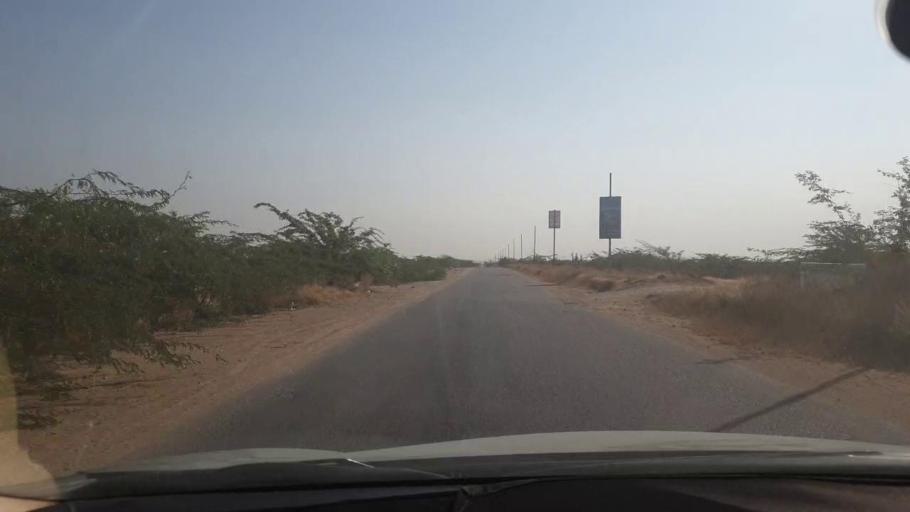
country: PK
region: Sindh
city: Malir Cantonment
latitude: 25.0687
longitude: 67.1388
